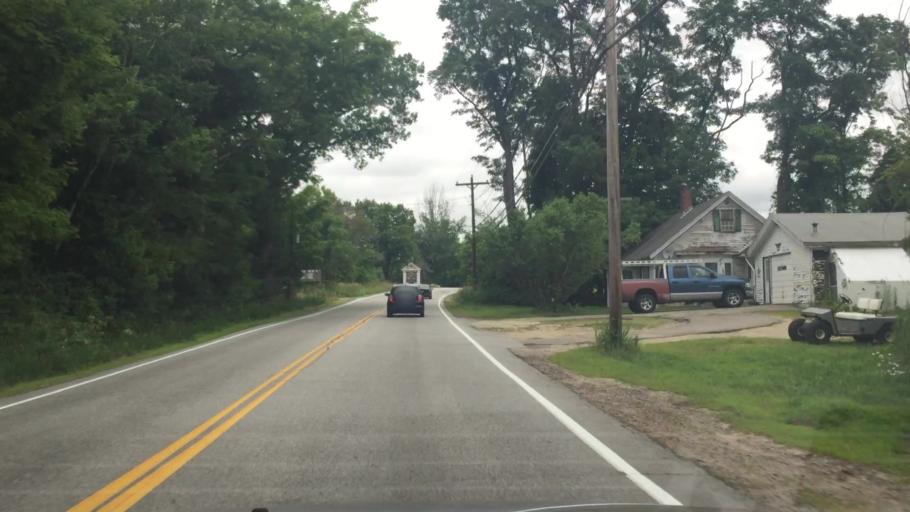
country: US
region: New Hampshire
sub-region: Belknap County
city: Meredith
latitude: 43.6711
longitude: -71.4867
